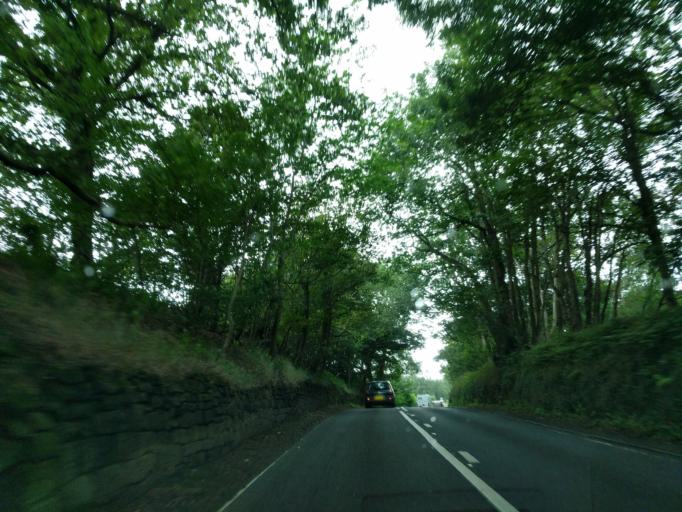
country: GB
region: England
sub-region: Staffordshire
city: Colwich
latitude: 52.7862
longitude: -2.0066
